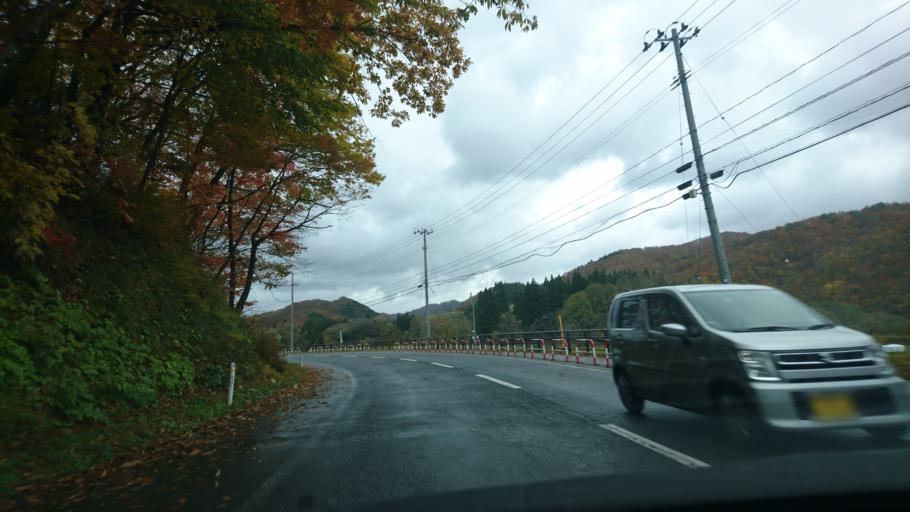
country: JP
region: Iwate
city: Shizukuishi
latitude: 39.5087
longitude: 140.8276
